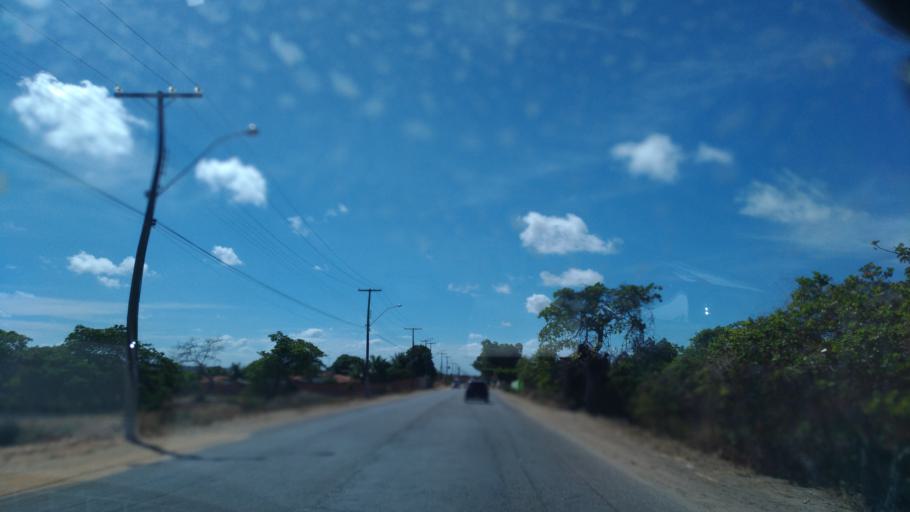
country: BR
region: Alagoas
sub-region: Marechal Deodoro
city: Marechal Deodoro
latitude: -9.7632
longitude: -35.8601
